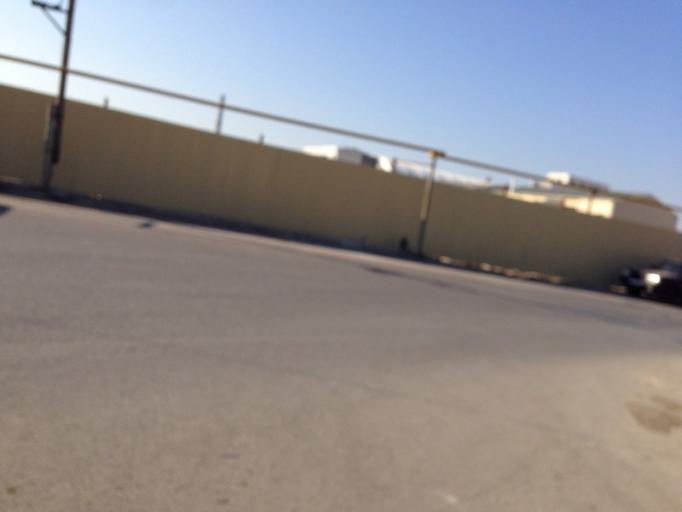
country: AZ
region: Baki
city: Baku
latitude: 40.4193
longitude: 49.8664
